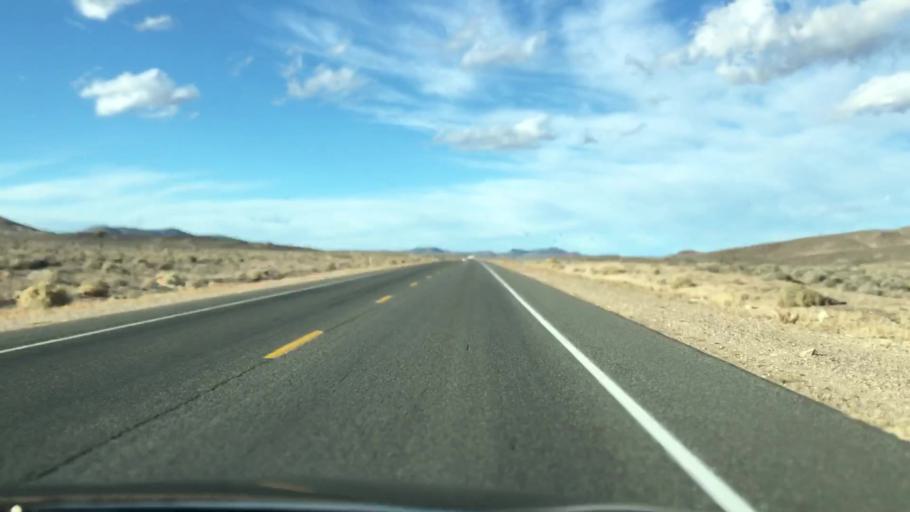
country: US
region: Nevada
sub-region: Esmeralda County
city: Goldfield
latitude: 37.5338
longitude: -117.1935
